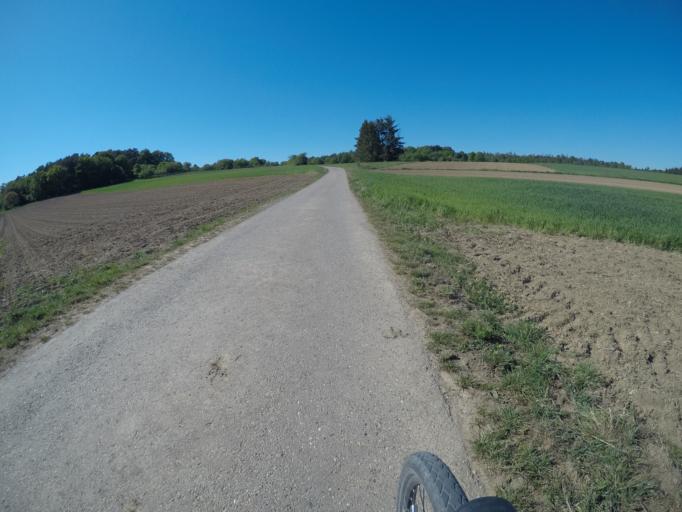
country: DE
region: Baden-Wuerttemberg
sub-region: Karlsruhe Region
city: Heimsheim
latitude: 48.8217
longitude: 8.8523
